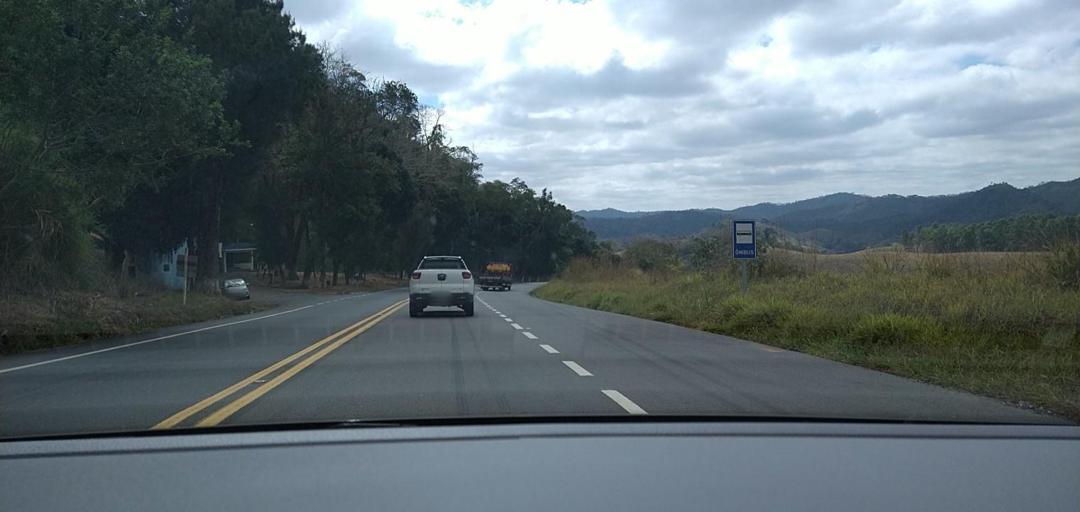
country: BR
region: Minas Gerais
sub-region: Ponte Nova
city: Ponte Nova
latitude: -20.5105
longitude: -42.8839
